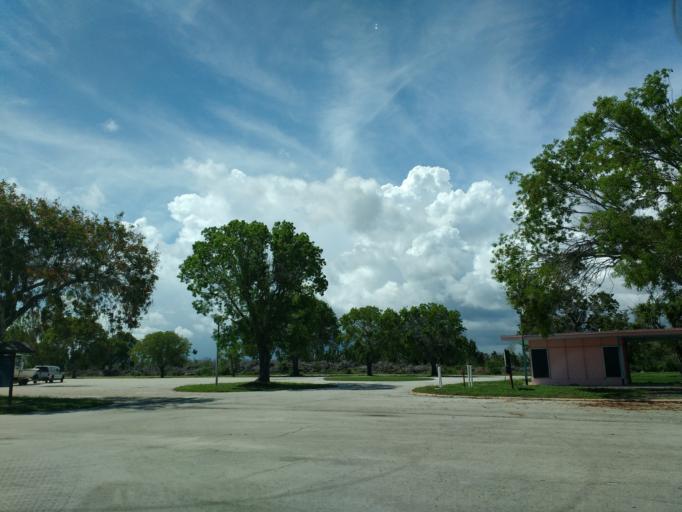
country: US
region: Florida
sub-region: Monroe County
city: Islamorada
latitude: 25.1438
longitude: -80.9227
